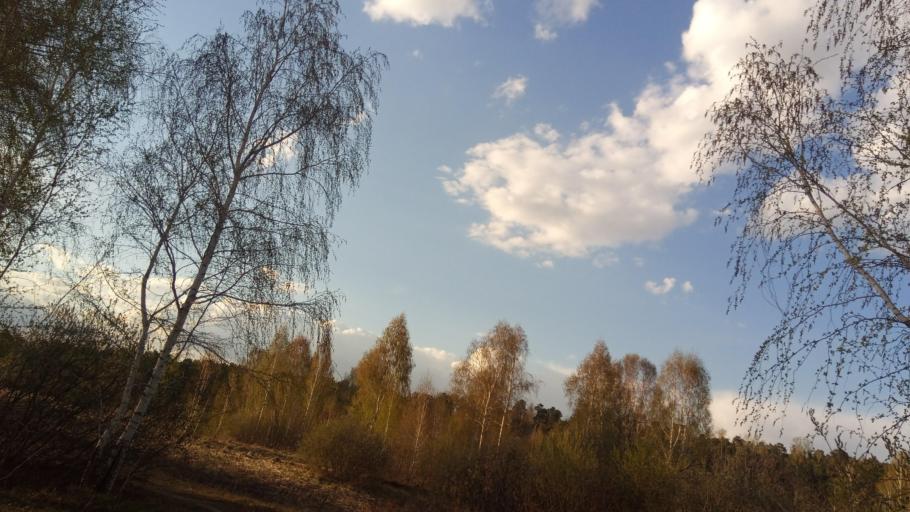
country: RU
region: Chelyabinsk
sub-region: Gorod Chelyabinsk
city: Chelyabinsk
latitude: 55.1575
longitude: 61.3211
